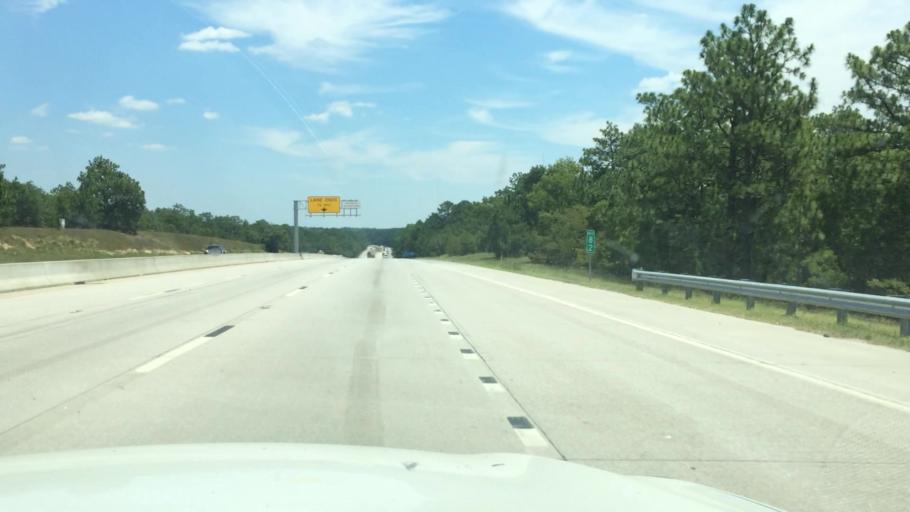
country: US
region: South Carolina
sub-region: Kershaw County
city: Elgin
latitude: 34.1063
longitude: -80.8242
